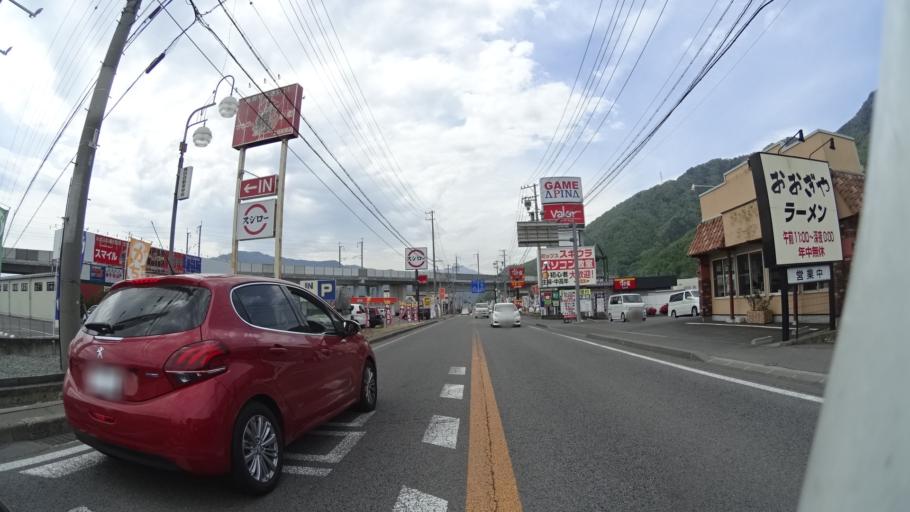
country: JP
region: Nagano
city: Ueda
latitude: 36.4153
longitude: 138.2237
